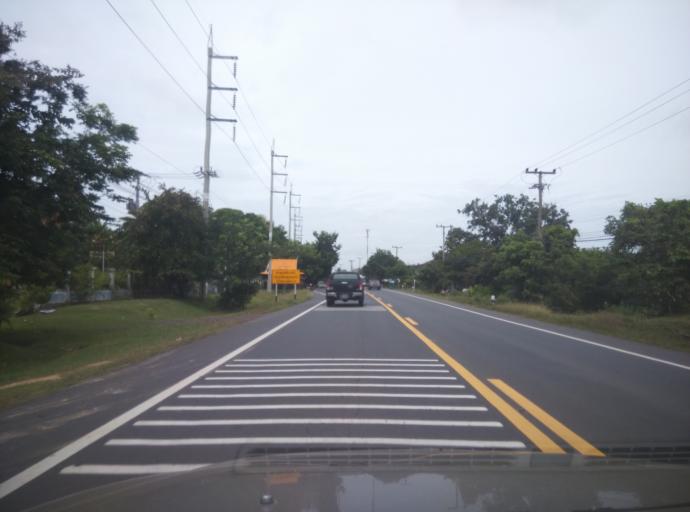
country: TH
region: Sisaket
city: Uthumphon Phisai
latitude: 15.0777
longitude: 104.1033
